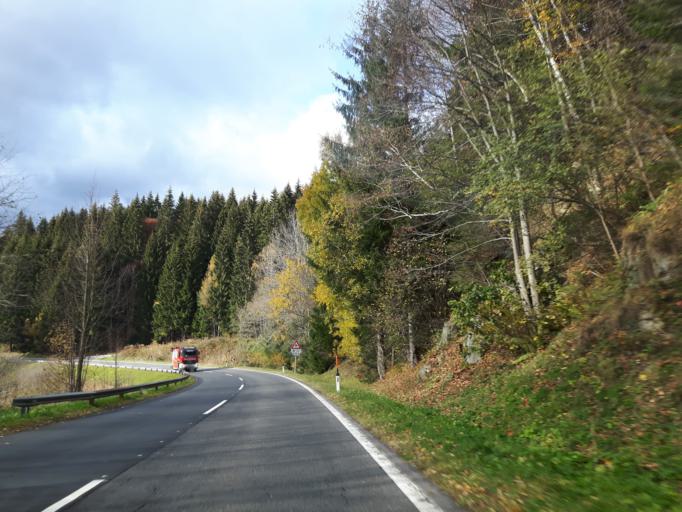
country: AT
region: Styria
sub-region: Politischer Bezirk Deutschlandsberg
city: Soboth
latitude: 46.7081
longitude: 15.0971
